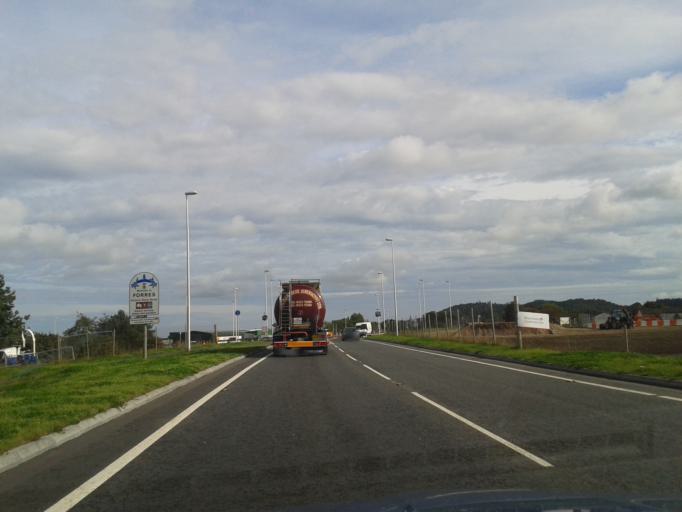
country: GB
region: Scotland
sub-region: Moray
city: Forres
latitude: 57.6053
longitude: -3.6406
